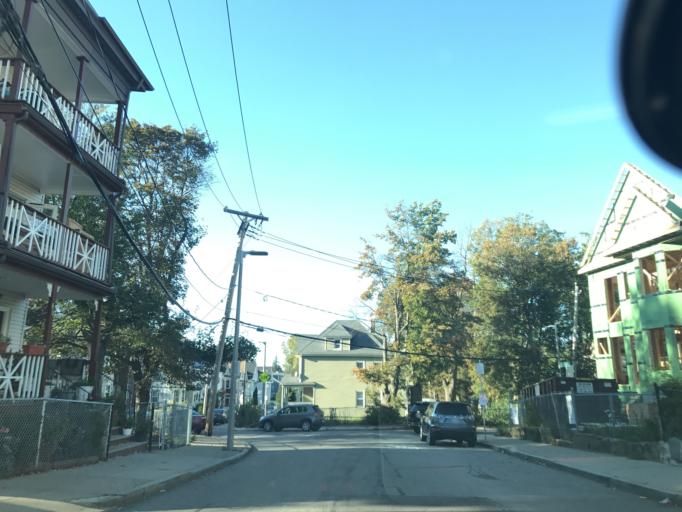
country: US
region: Massachusetts
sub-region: Norfolk County
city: Milton
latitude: 42.2828
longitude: -71.0856
